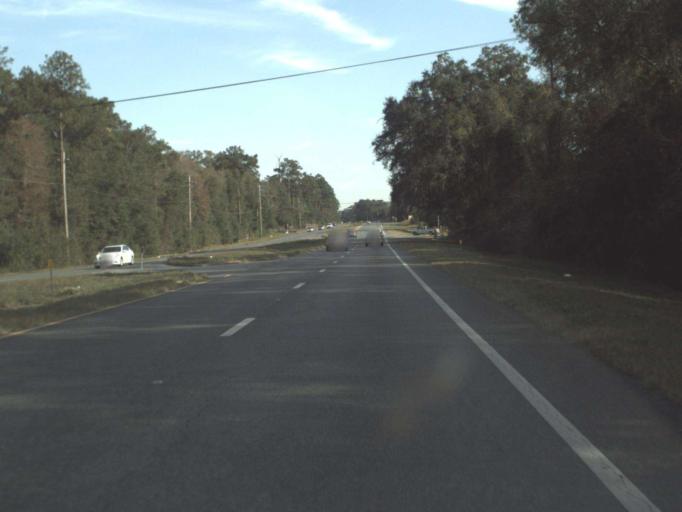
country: US
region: Florida
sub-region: Gadsden County
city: Midway
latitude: 30.4641
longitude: -84.3948
